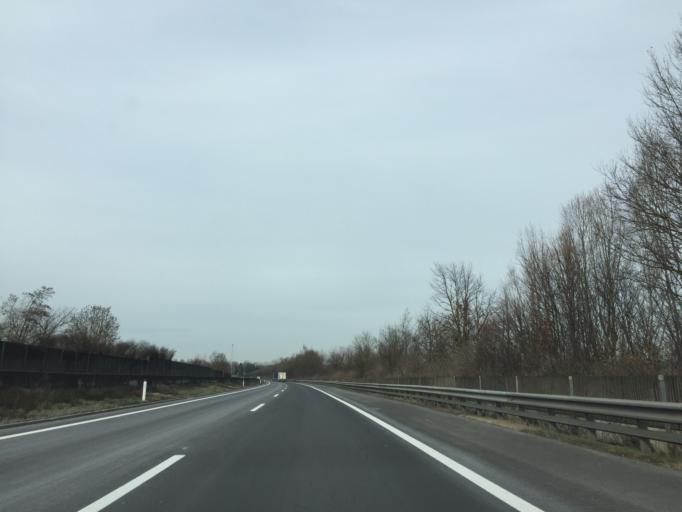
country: AT
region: Upper Austria
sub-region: Politischer Bezirk Scharding
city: Sankt Marienkirchen bei Schaerding
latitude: 48.3006
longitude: 13.4744
